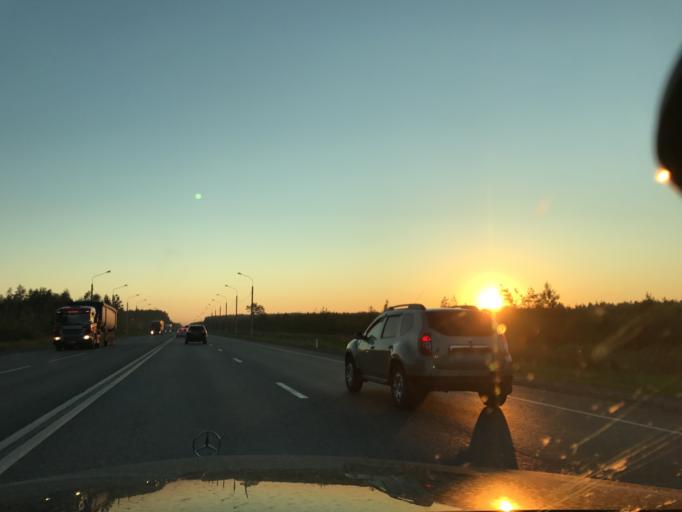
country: RU
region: Vladimir
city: Pokrov
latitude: 55.9239
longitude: 39.2578
